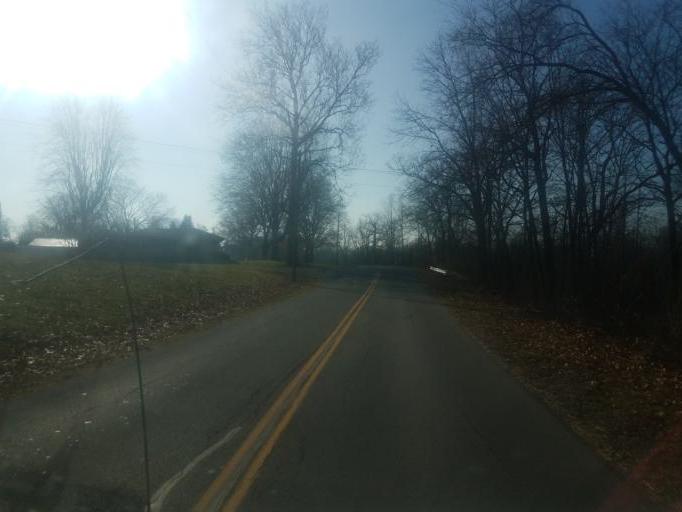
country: US
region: Ohio
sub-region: Seneca County
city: Tiffin
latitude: 41.1281
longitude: -83.1659
